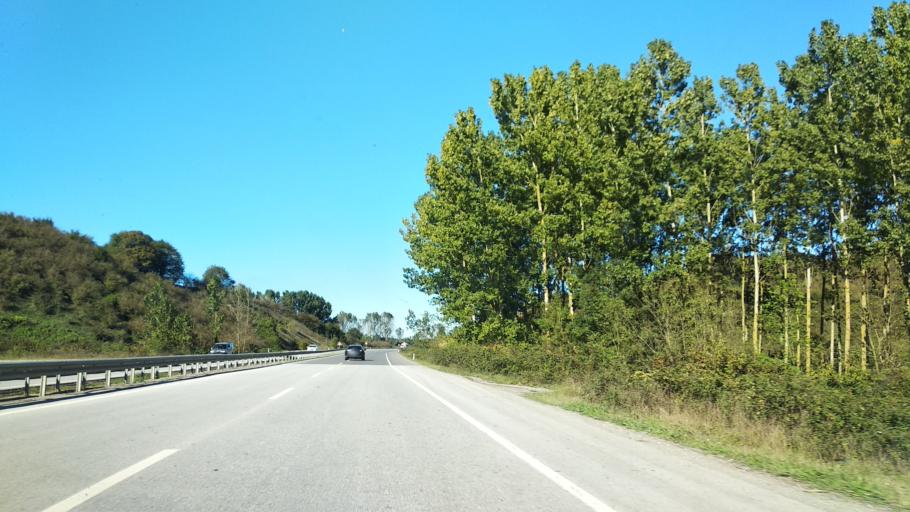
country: TR
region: Sakarya
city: Karasu
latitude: 41.0584
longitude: 30.6367
